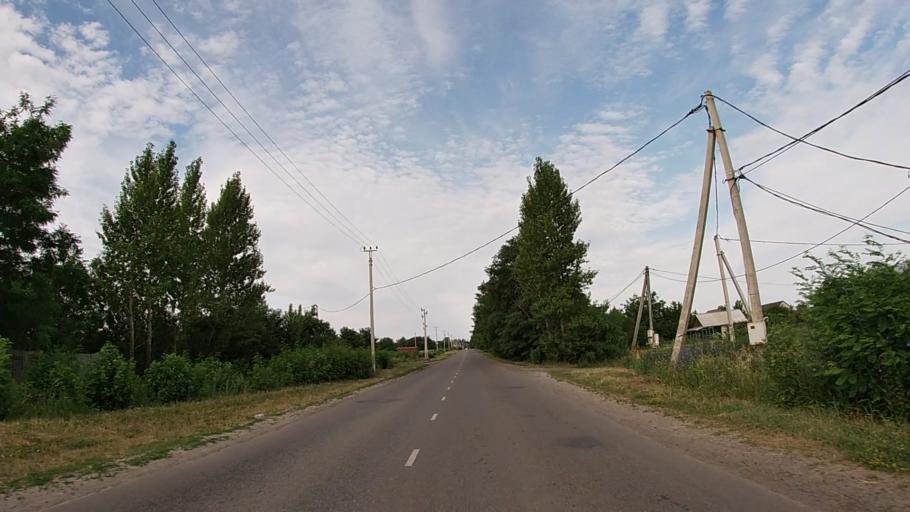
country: RU
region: Belgorod
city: Severnyy
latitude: 50.6934
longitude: 36.5679
